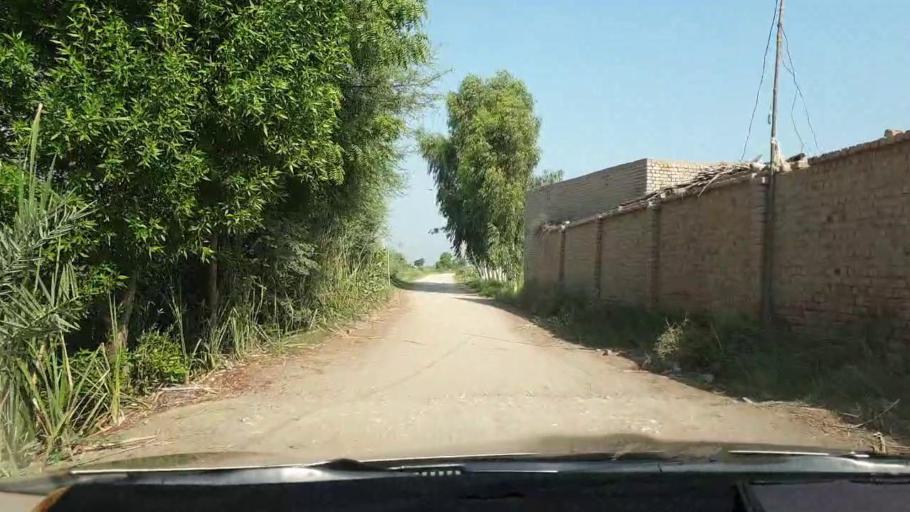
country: PK
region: Sindh
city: Larkana
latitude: 27.6315
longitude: 68.2390
